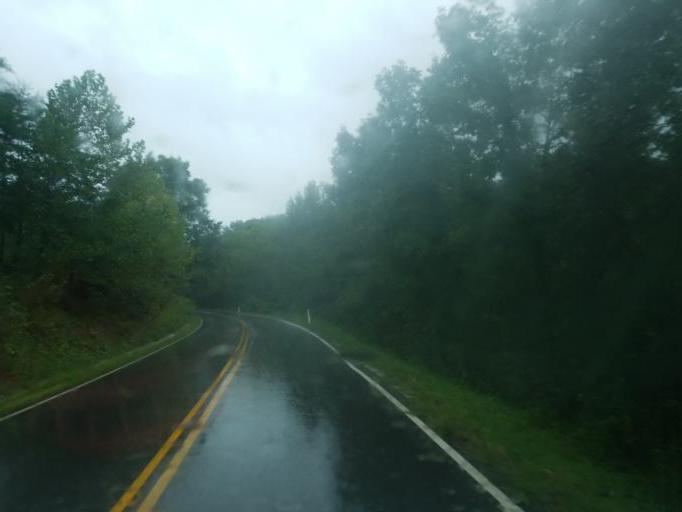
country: US
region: Kentucky
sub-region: Carter County
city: Grayson
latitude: 38.4943
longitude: -82.9938
